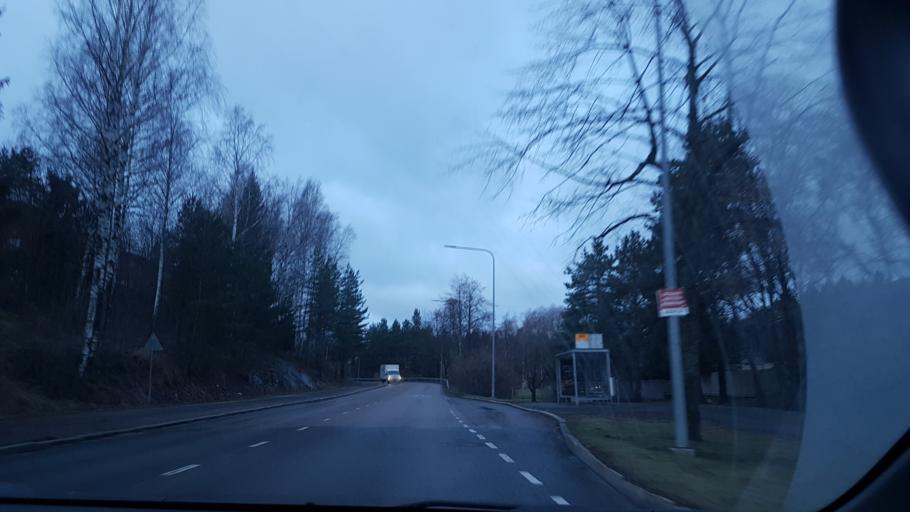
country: FI
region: Uusimaa
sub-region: Helsinki
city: Vantaa
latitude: 60.2810
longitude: 25.1158
